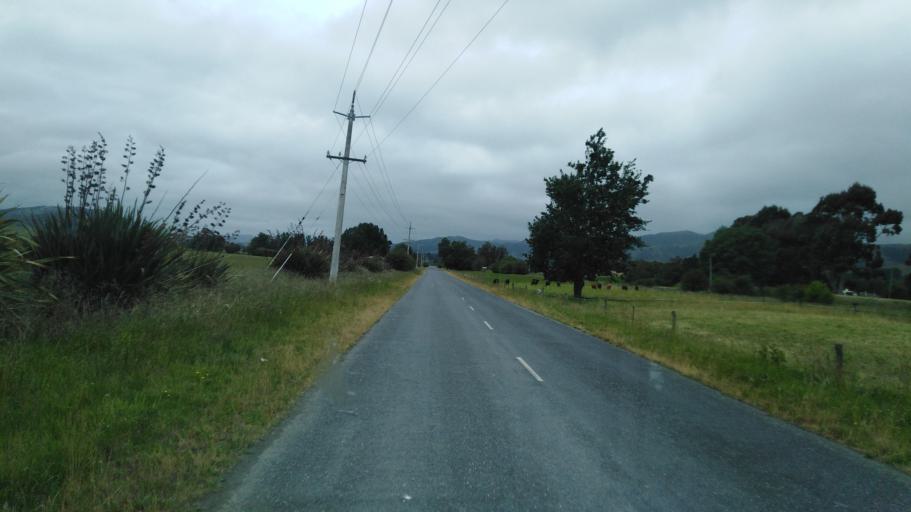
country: NZ
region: Canterbury
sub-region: Kaikoura District
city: Kaikoura
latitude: -42.7089
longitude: 173.2928
